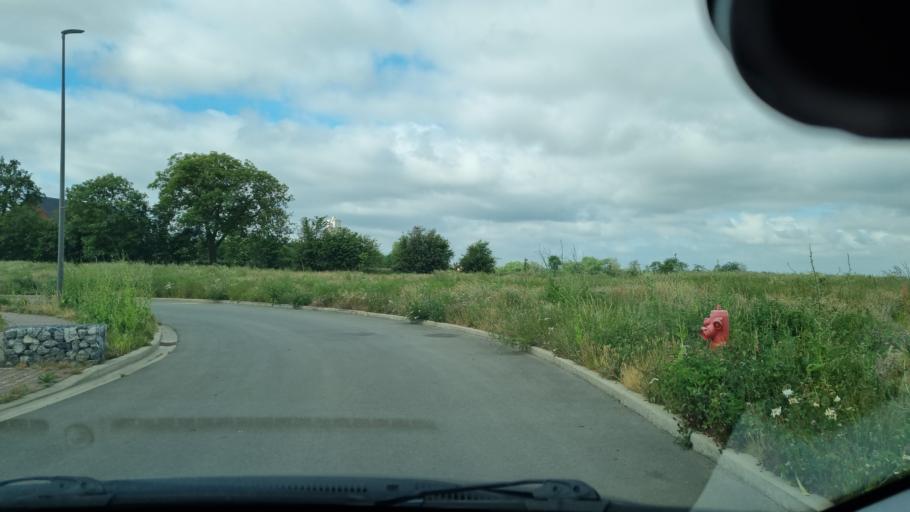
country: BE
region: Wallonia
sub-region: Province de Liege
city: Bassenge
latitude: 50.7383
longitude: 5.6023
